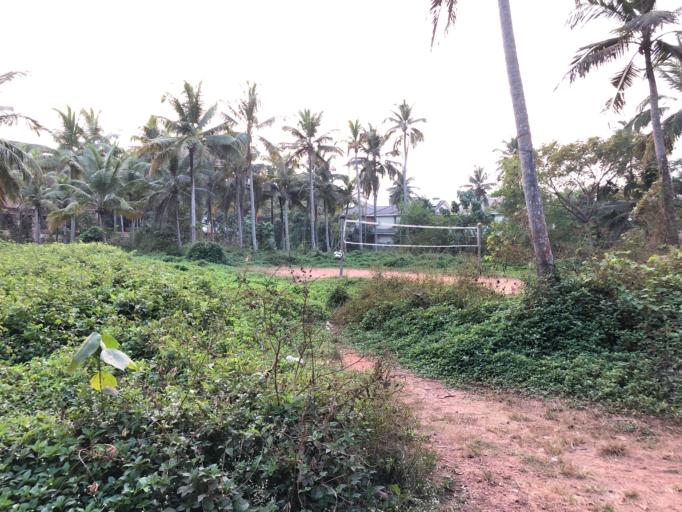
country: IN
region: Karnataka
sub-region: Dakshina Kannada
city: Mangalore
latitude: 12.8899
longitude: 74.8663
